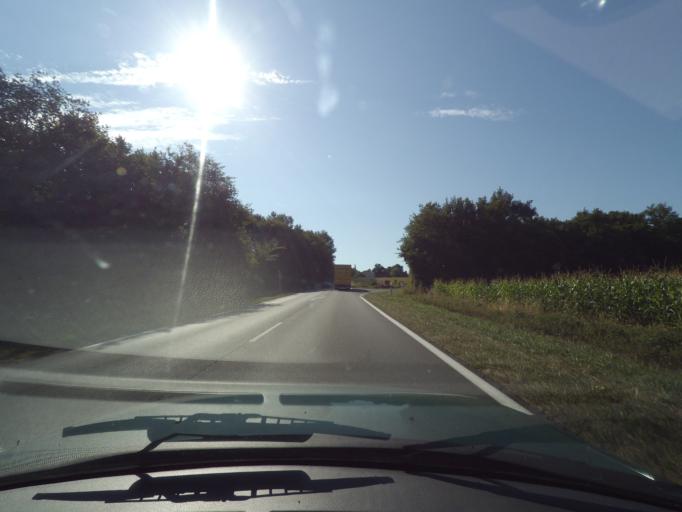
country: FR
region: Poitou-Charentes
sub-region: Departement de la Vienne
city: Terce
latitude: 46.4447
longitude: 0.5785
